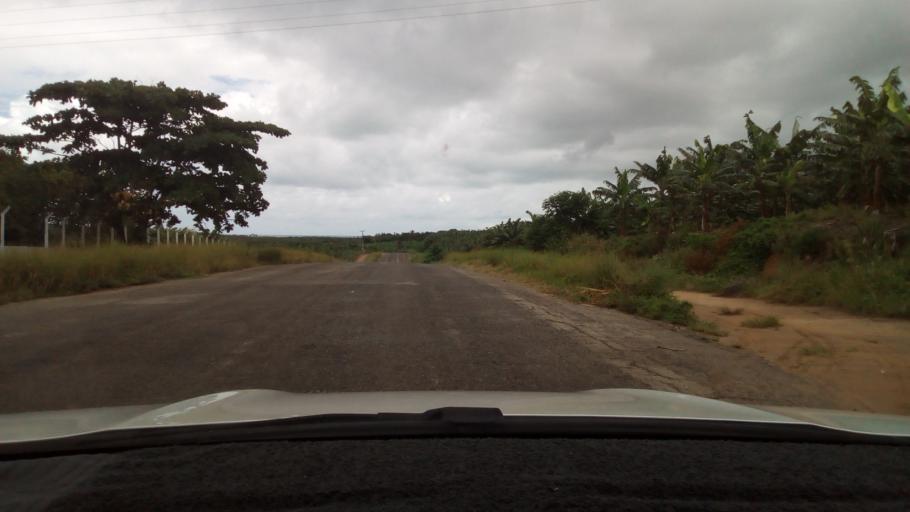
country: BR
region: Paraiba
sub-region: Pitimbu
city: Pitimbu
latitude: -7.3556
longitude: -34.8215
